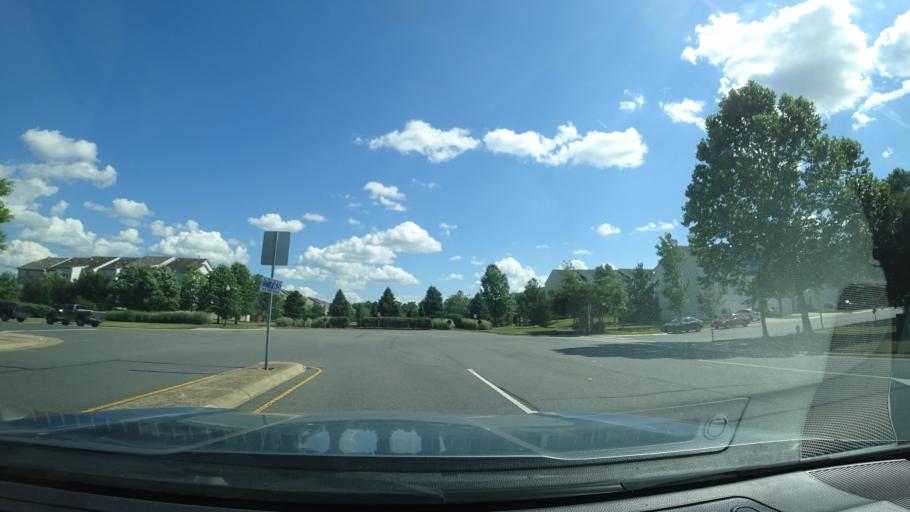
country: US
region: Virginia
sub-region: Loudoun County
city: Broadlands
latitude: 38.9905
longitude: -77.4860
